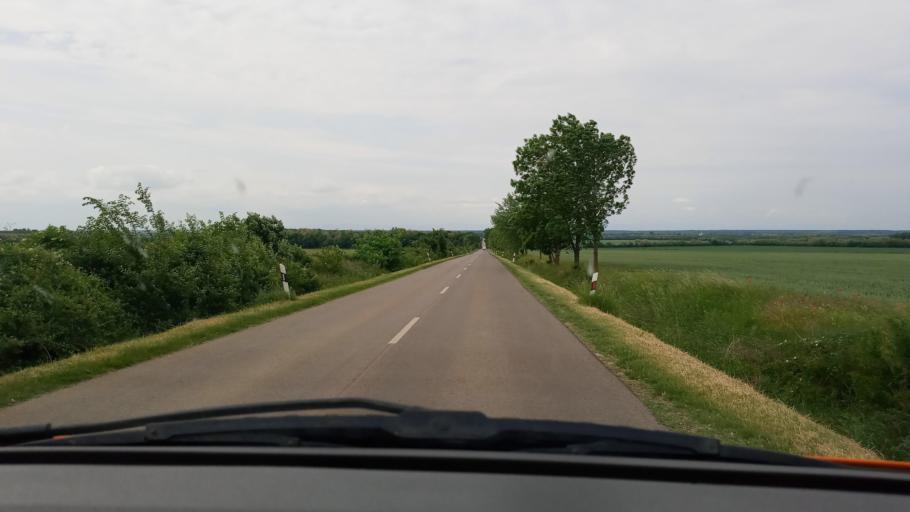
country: HU
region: Baranya
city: Vajszlo
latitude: 45.9330
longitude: 18.0682
